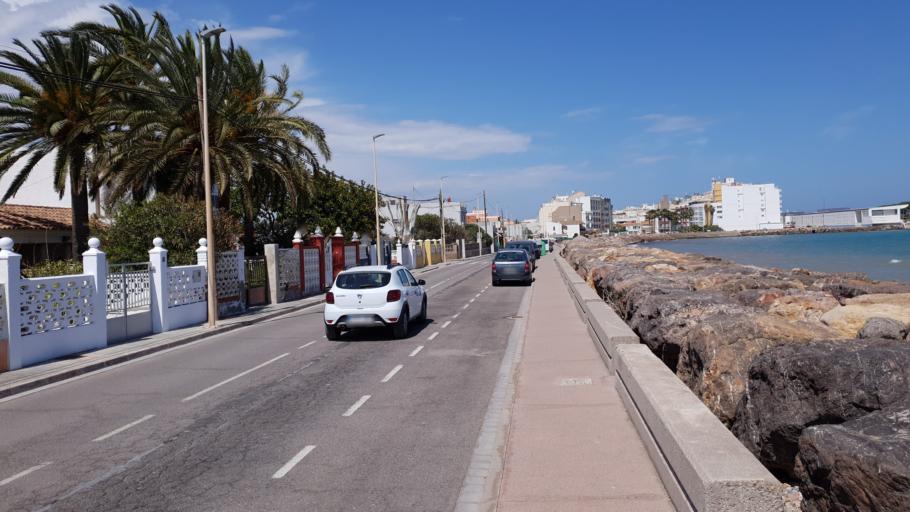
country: ES
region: Valencia
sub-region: Provincia de Castello
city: Burriana
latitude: 39.8610
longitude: -0.0808
